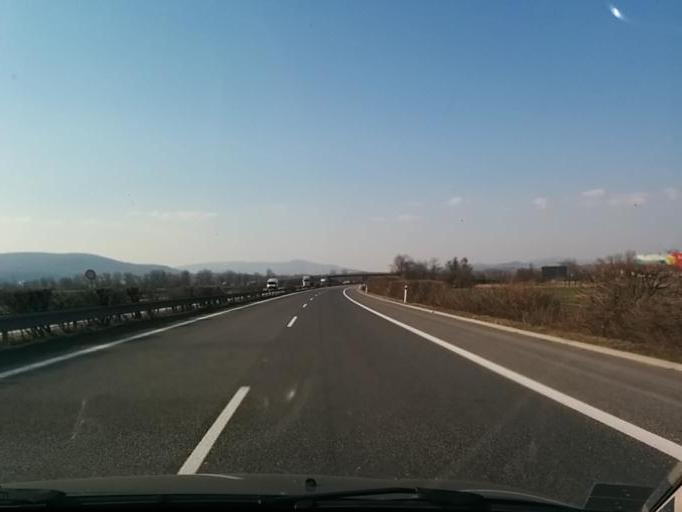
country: SK
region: Trenciansky
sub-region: Okres Nove Mesto nad Vahom
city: Nove Mesto nad Vahom
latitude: 48.7340
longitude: 17.8663
